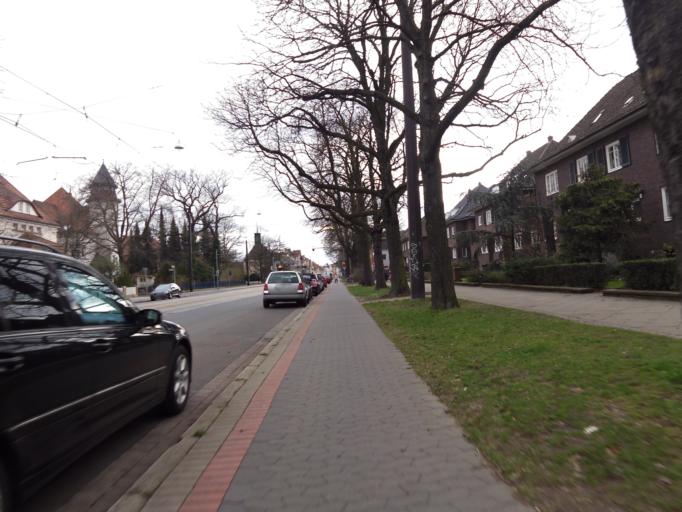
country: DE
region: Lower Saxony
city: Laatzen
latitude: 52.3714
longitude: 9.7954
